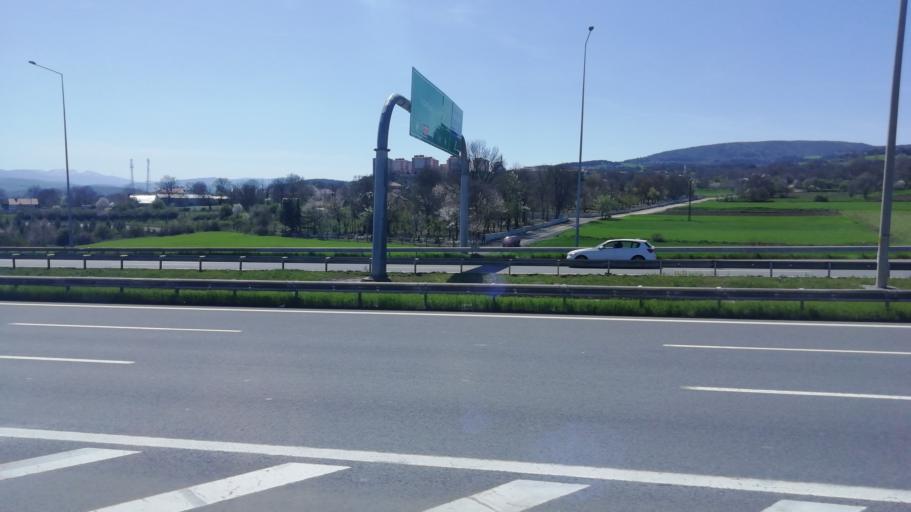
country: TR
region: Bolu
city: Bolu
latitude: 40.7448
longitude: 31.5615
